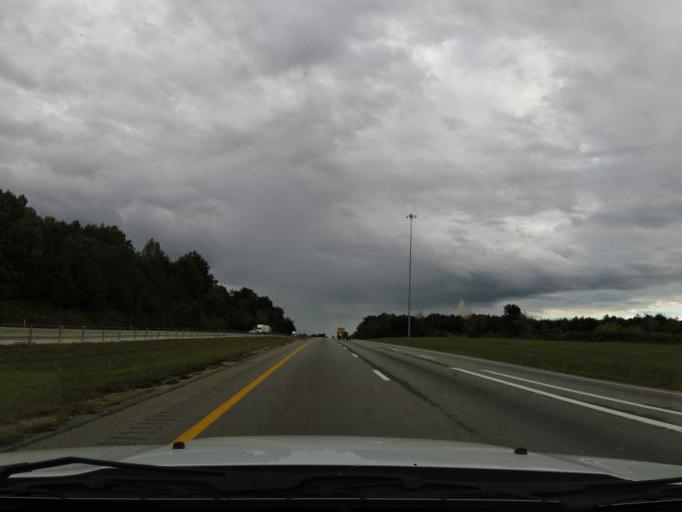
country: US
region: Kentucky
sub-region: Laurel County
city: North Corbin
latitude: 36.9801
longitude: -84.1104
